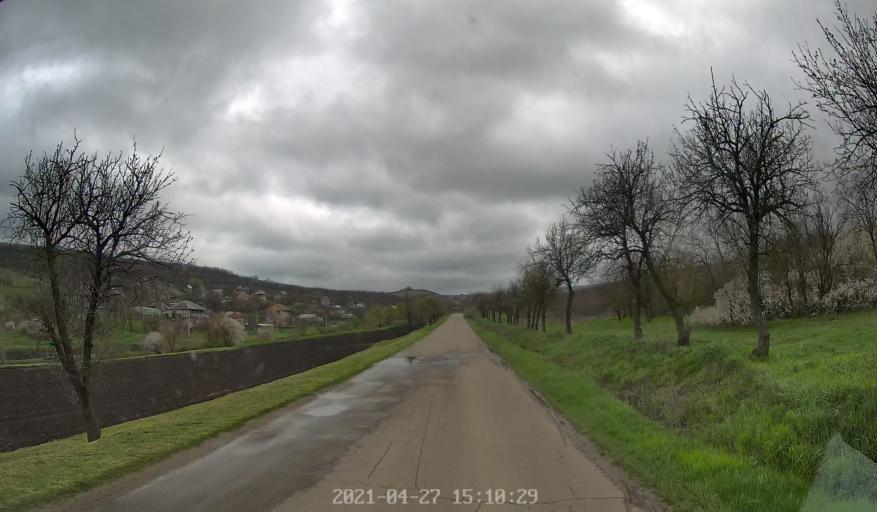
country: MD
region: Chisinau
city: Vadul lui Voda
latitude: 47.0401
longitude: 29.0327
